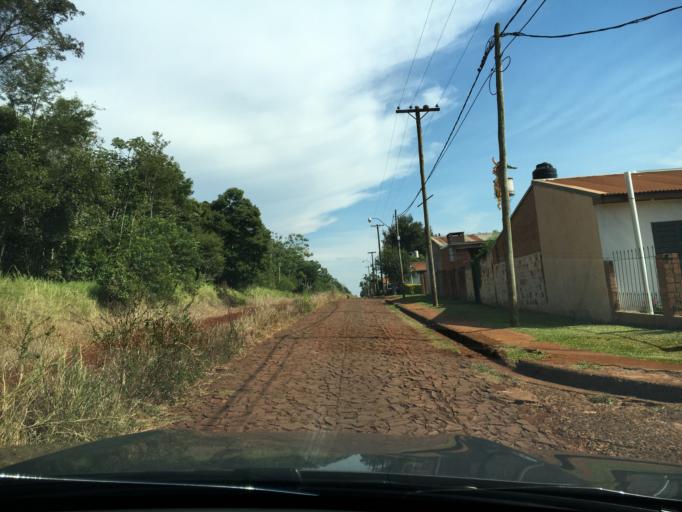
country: AR
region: Misiones
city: Puerto Rico
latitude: -26.8047
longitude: -54.9997
